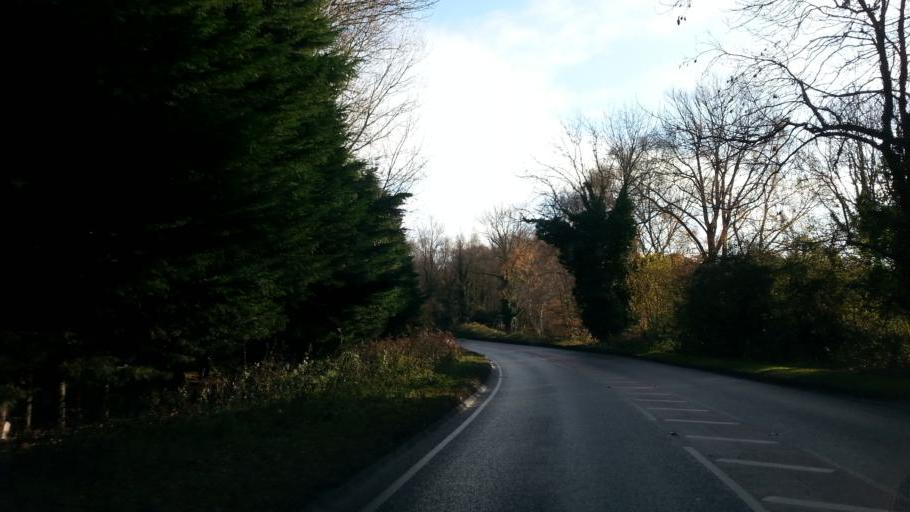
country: GB
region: England
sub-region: Suffolk
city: Woodbridge
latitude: 52.1018
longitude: 1.3575
